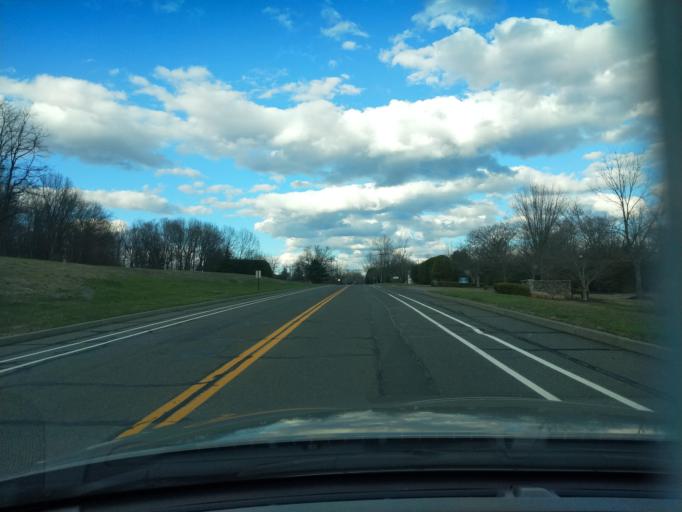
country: US
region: Connecticut
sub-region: Fairfield County
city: Bethel
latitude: 41.4249
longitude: -73.3980
